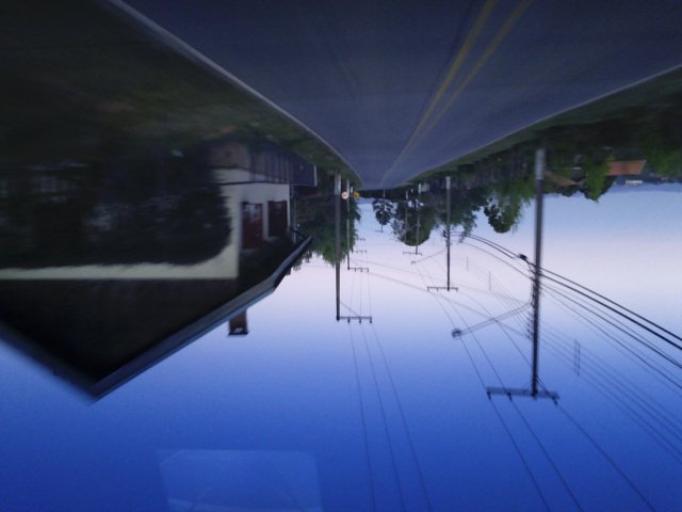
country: BR
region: Sao Paulo
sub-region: Campos Do Jordao
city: Campos do Jordao
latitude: -22.7345
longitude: -45.6080
